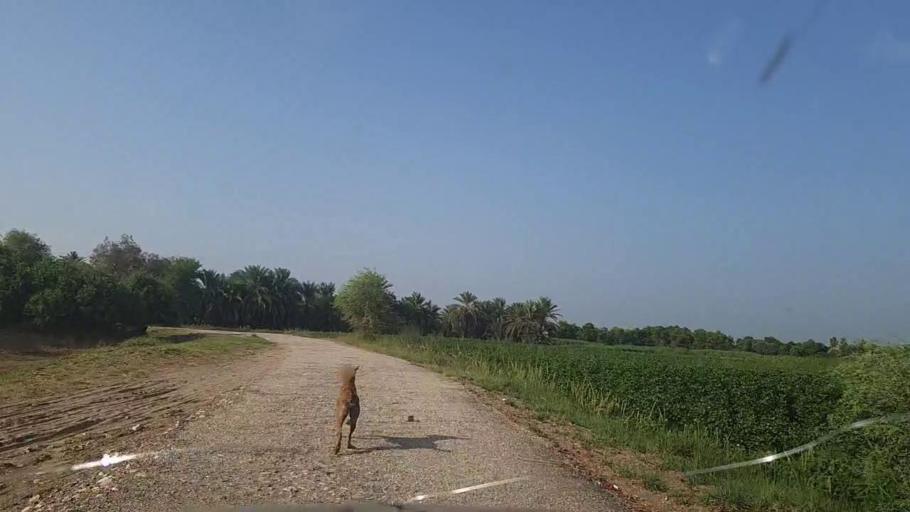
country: PK
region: Sindh
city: Khanpur
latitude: 27.7235
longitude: 69.3319
